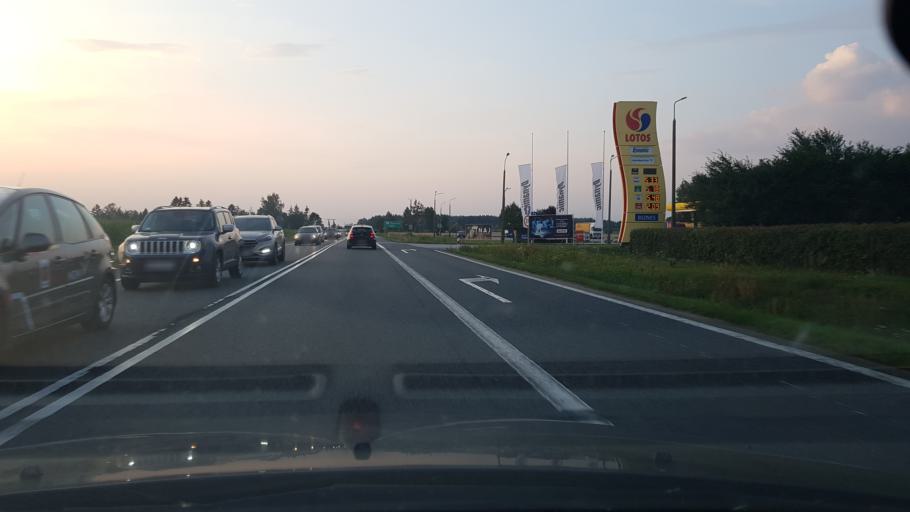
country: PL
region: Masovian Voivodeship
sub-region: Powiat mlawski
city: Wieczfnia Koscielna
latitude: 53.1996
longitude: 20.4360
